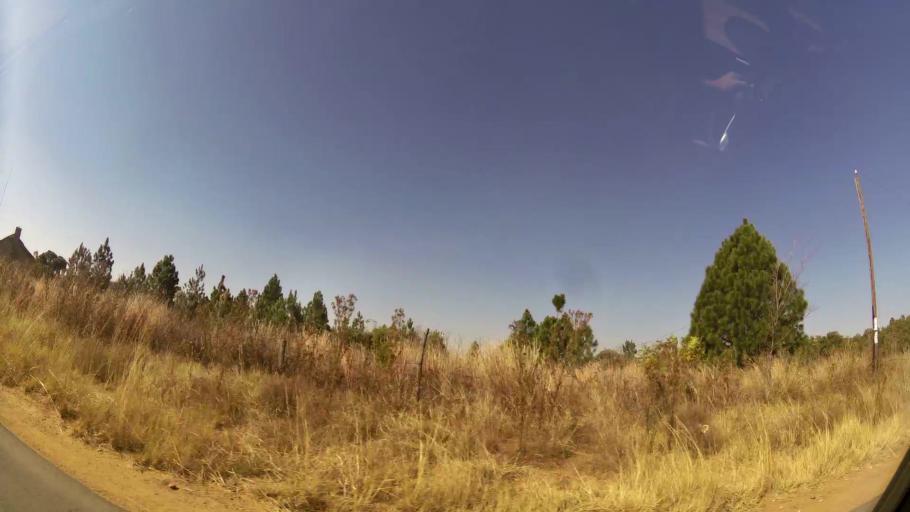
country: ZA
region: Gauteng
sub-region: City of Johannesburg Metropolitan Municipality
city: Diepsloot
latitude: -25.9269
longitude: 28.0756
